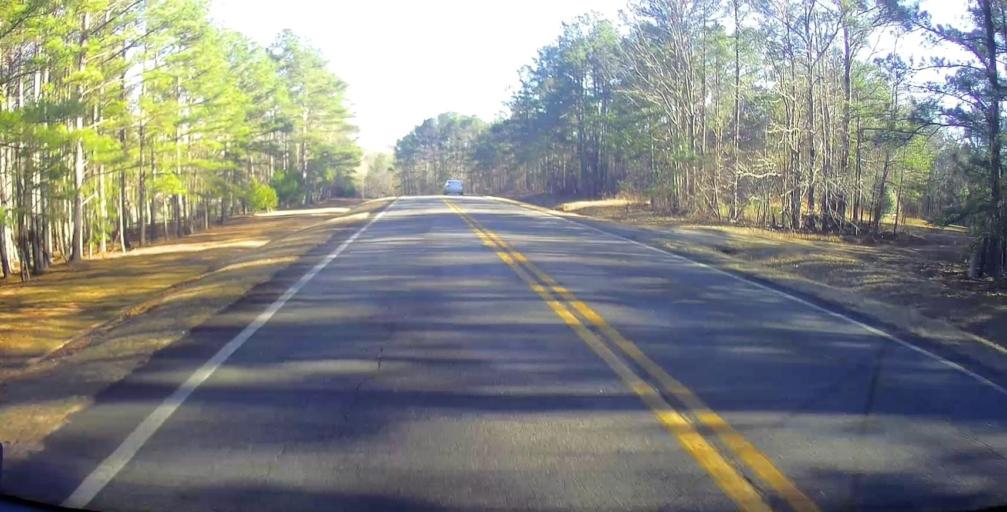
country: US
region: Georgia
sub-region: Talbot County
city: Sardis
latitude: 32.7803
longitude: -84.6842
